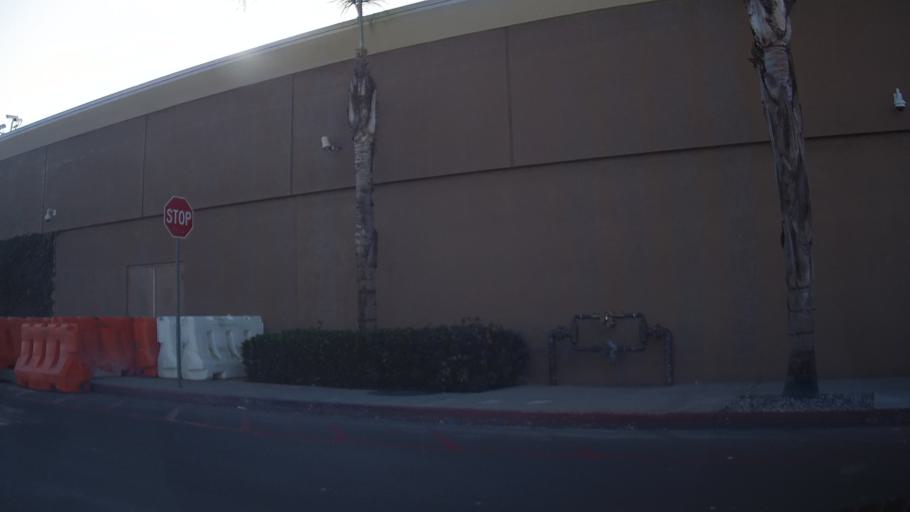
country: US
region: California
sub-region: San Diego County
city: La Mesa
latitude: 32.7774
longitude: -117.0086
